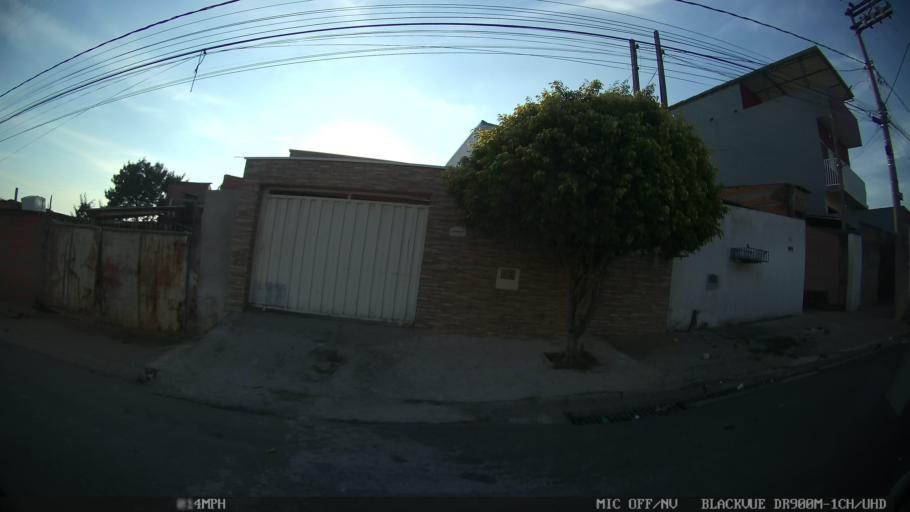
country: BR
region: Sao Paulo
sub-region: Campinas
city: Campinas
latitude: -22.9945
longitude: -47.1169
